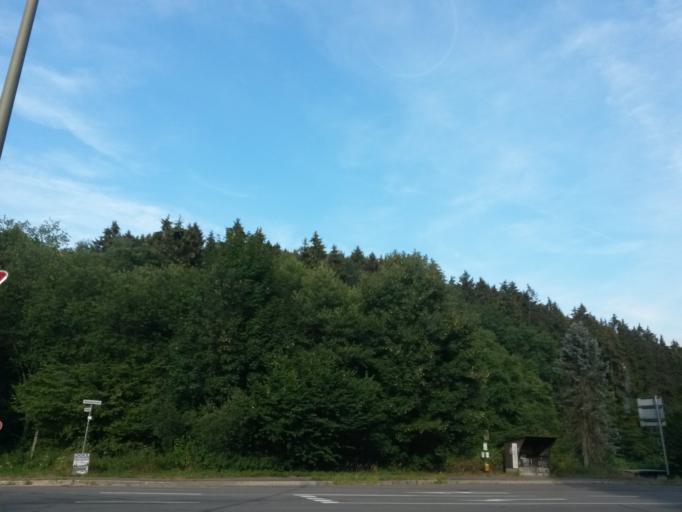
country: DE
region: North Rhine-Westphalia
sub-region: Regierungsbezirk Koln
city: Lindlar
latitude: 51.0371
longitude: 7.4281
